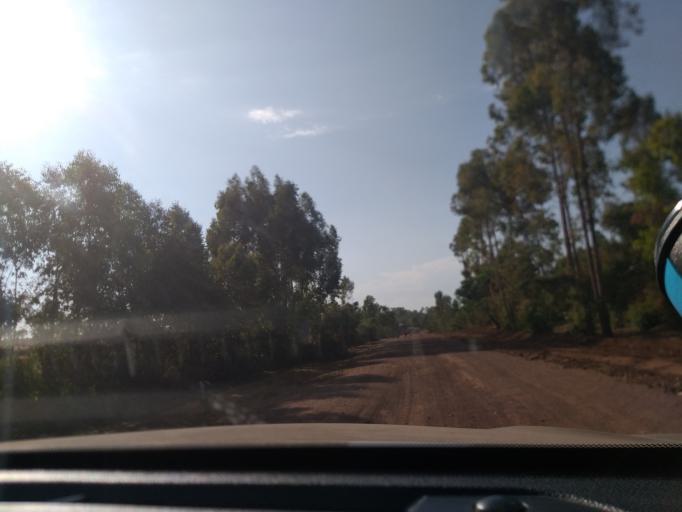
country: ET
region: Oromiya
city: Shashemene
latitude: 7.4288
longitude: 38.8070
